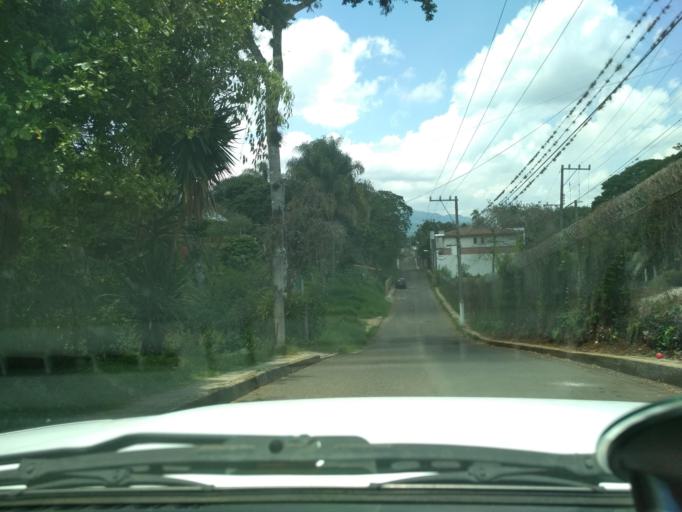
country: MX
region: Veracruz
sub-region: Cordoba
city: San Jose de Abajo [Unidad Habitacional]
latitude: 18.9147
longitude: -96.9583
